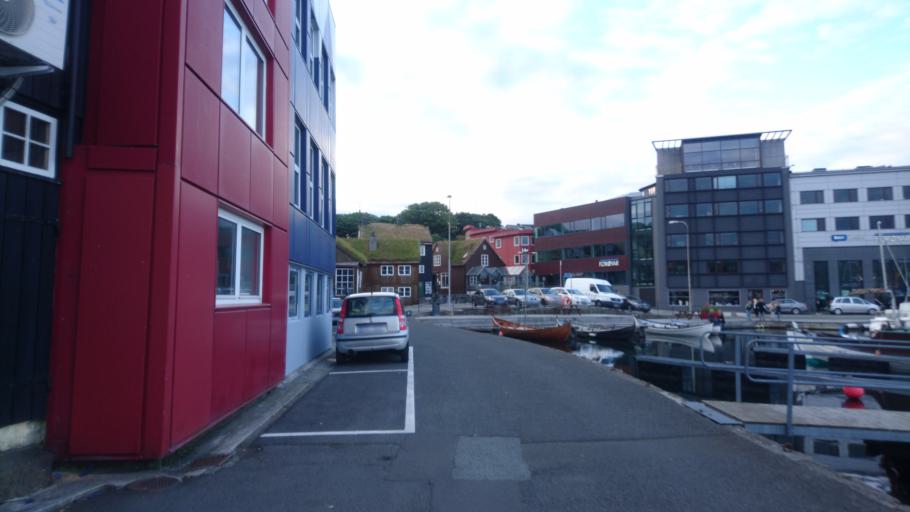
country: FO
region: Streymoy
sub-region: Torshavn
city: Torshavn
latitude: 62.0087
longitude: -6.7694
